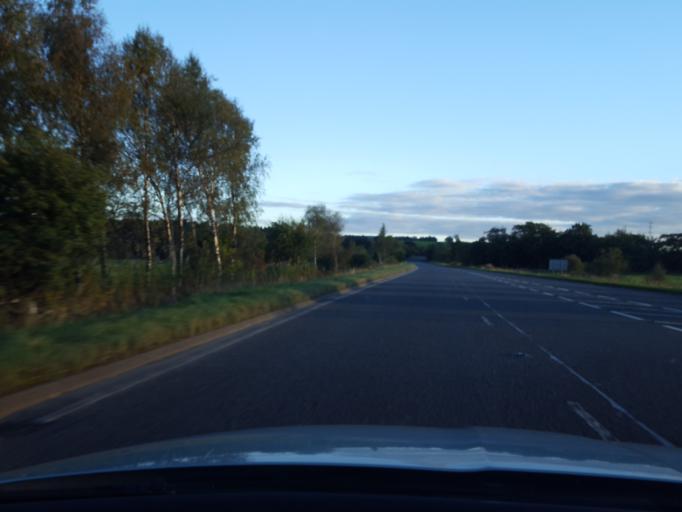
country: GB
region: Scotland
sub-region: West Lothian
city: Bathgate
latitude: 55.9158
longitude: -3.6766
